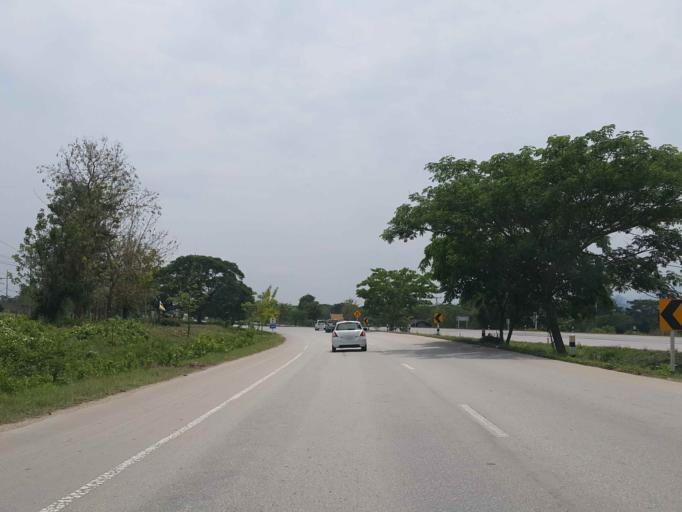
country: TH
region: Lampang
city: Sop Prap
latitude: 17.9398
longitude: 99.3491
